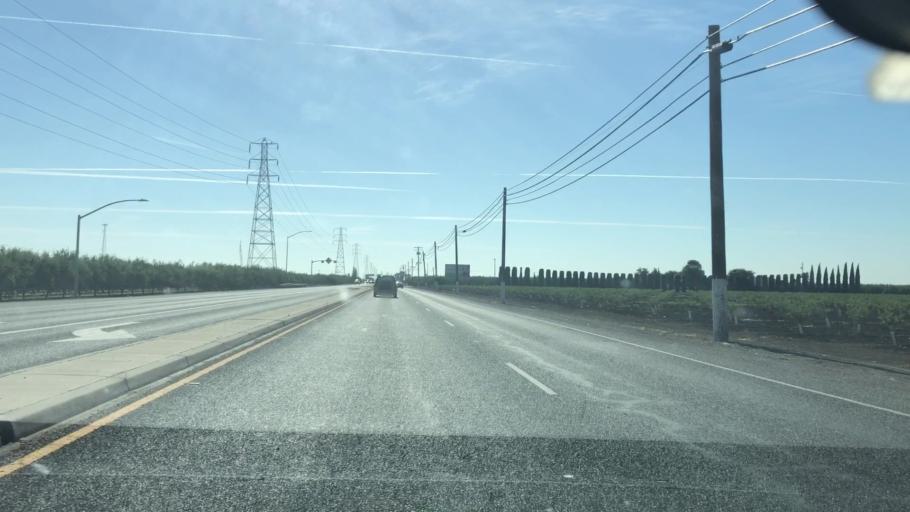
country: US
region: California
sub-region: San Joaquin County
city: Tracy
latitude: 37.7397
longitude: -121.3794
